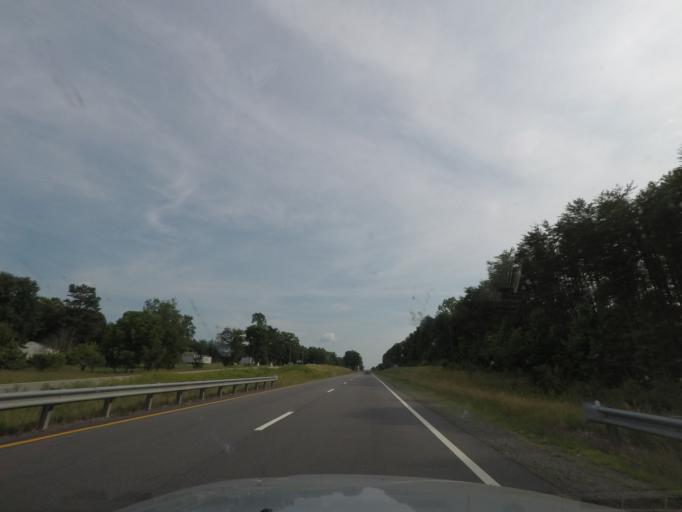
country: US
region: Virginia
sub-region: Mecklenburg County
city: Chase City
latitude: 36.9436
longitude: -78.5026
